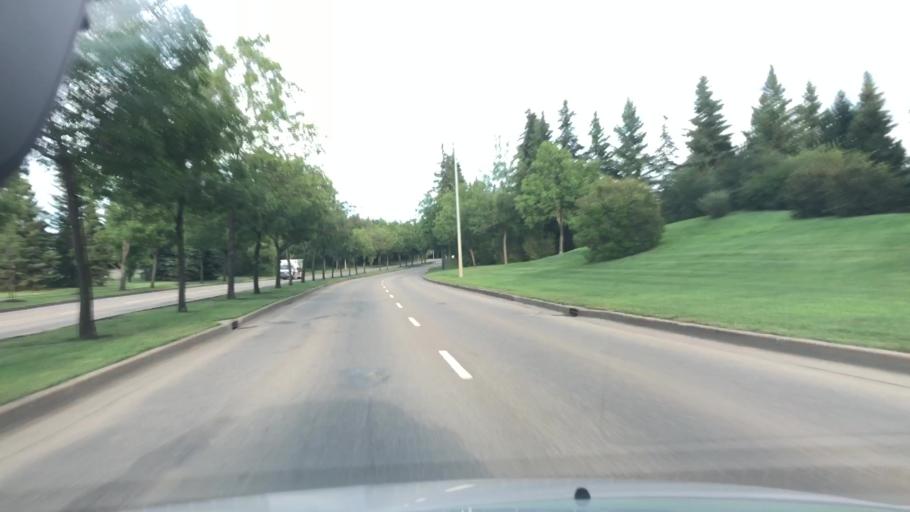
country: CA
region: Alberta
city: St. Albert
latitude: 53.6400
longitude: -113.5983
